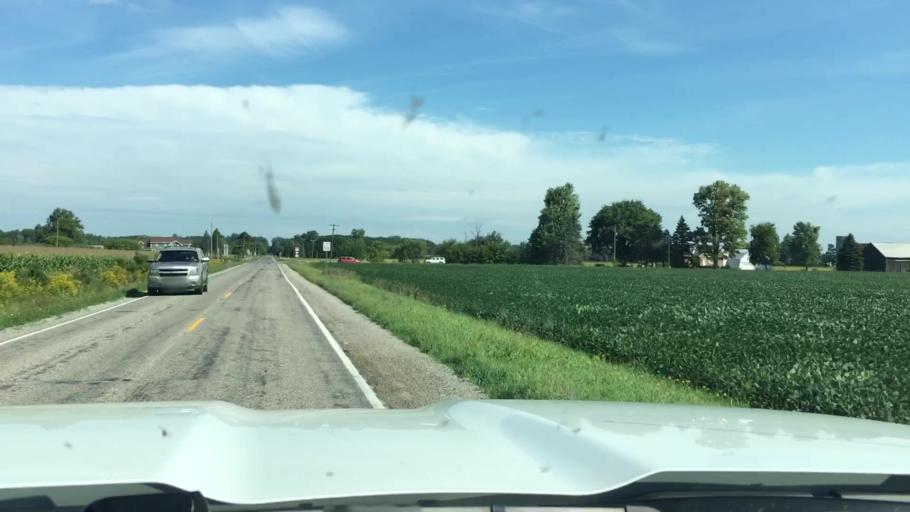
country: US
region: Michigan
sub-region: Saginaw County
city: Hemlock
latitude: 43.4488
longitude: -84.2301
